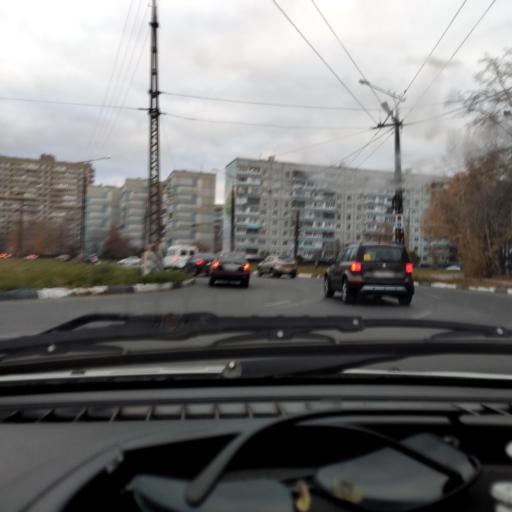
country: RU
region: Samara
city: Tol'yatti
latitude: 53.5051
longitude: 49.4337
